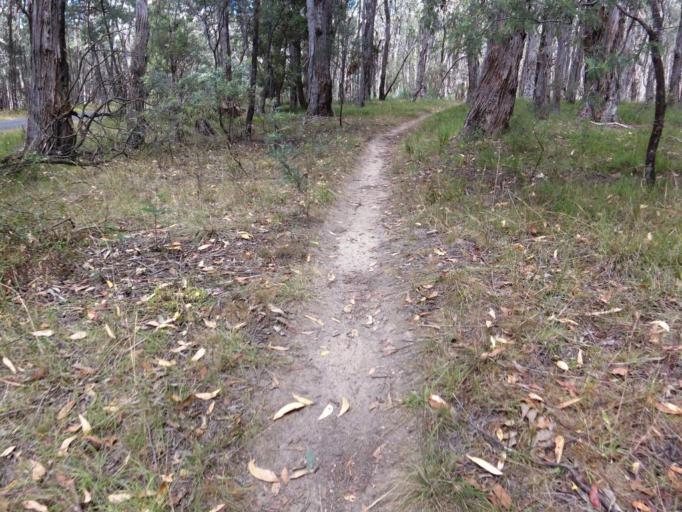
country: AU
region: Victoria
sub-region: Melton
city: Melton West
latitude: -37.4843
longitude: 144.5437
